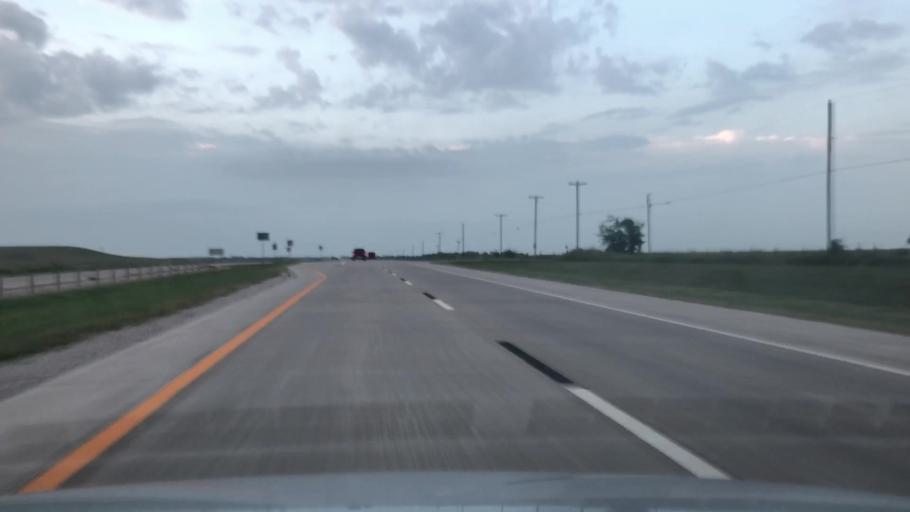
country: US
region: Oklahoma
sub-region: Osage County
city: Skiatook
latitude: 36.3790
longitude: -95.9202
